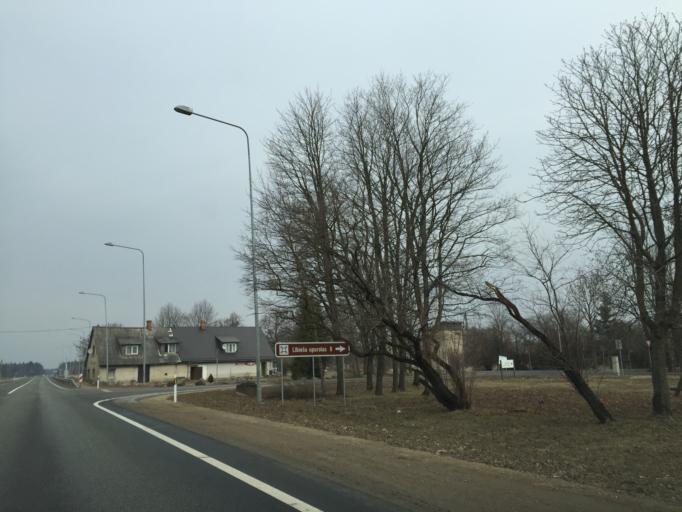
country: LV
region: Salacgrivas
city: Salacgriva
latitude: 57.7015
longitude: 24.3723
